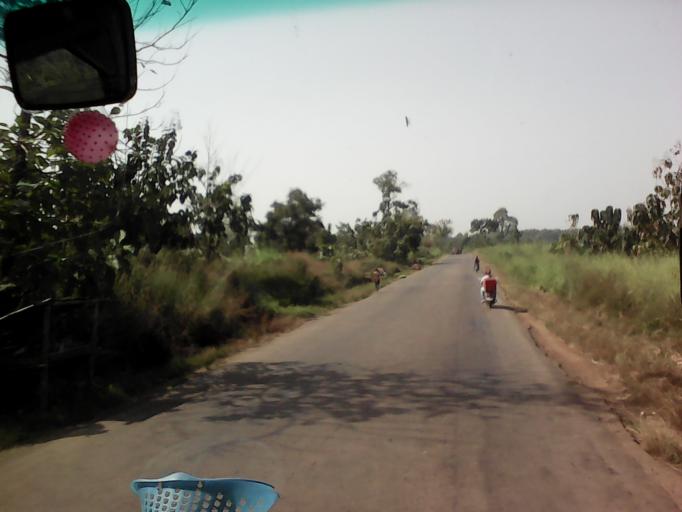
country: TG
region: Centrale
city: Sokode
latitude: 8.8741
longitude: 1.0810
